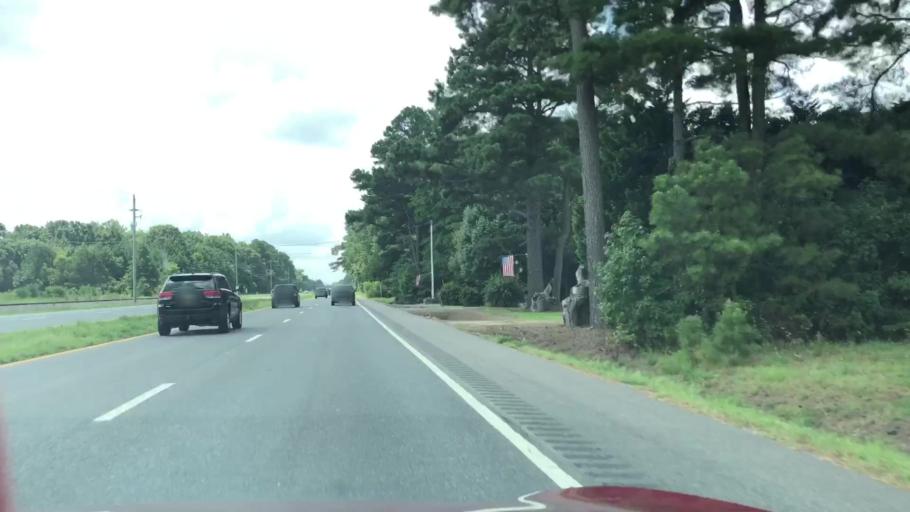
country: US
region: Virginia
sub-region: Northampton County
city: Eastville
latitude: 37.4354
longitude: -75.8851
